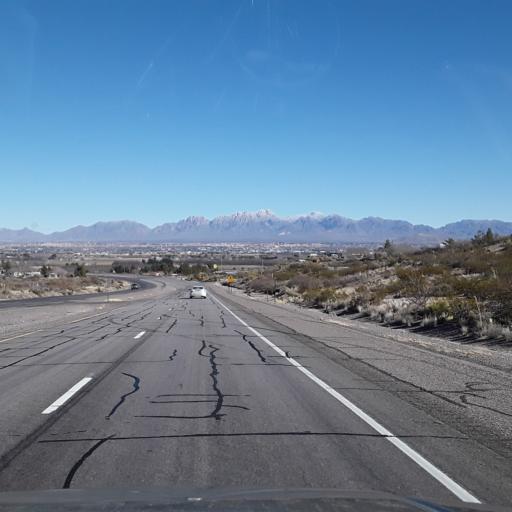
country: US
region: New Mexico
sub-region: Dona Ana County
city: Mesilla
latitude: 32.2923
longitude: -106.8653
